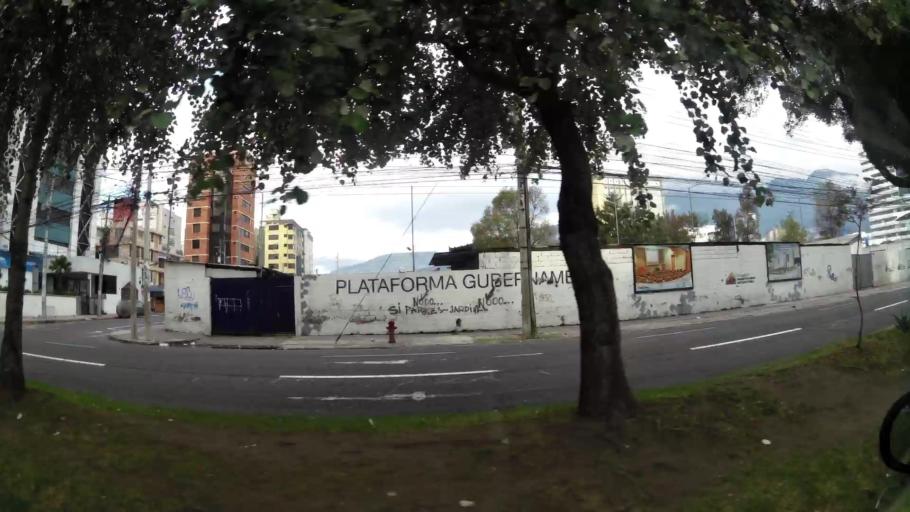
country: EC
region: Pichincha
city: Quito
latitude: -0.1924
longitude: -78.4857
